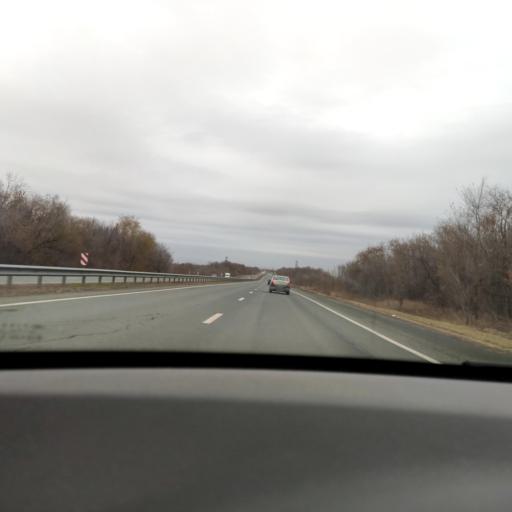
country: RU
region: Samara
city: Novokuybyshevsk
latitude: 53.0360
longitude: 49.9974
